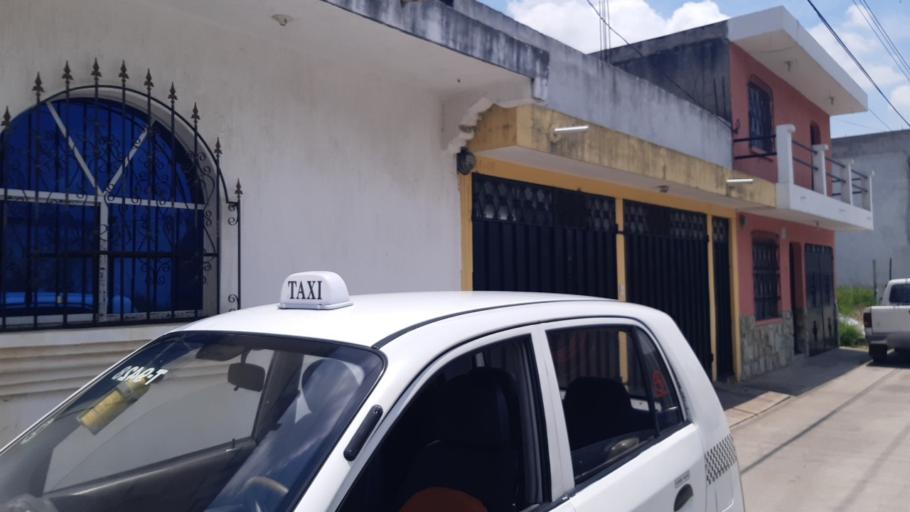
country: GT
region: Guatemala
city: Petapa
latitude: 14.5108
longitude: -90.5591
